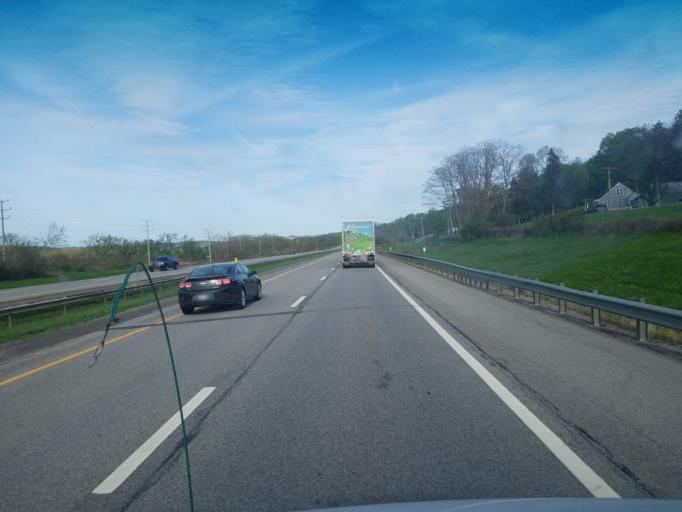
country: US
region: New York
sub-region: Herkimer County
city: Herkimer
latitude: 43.0141
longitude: -74.9371
